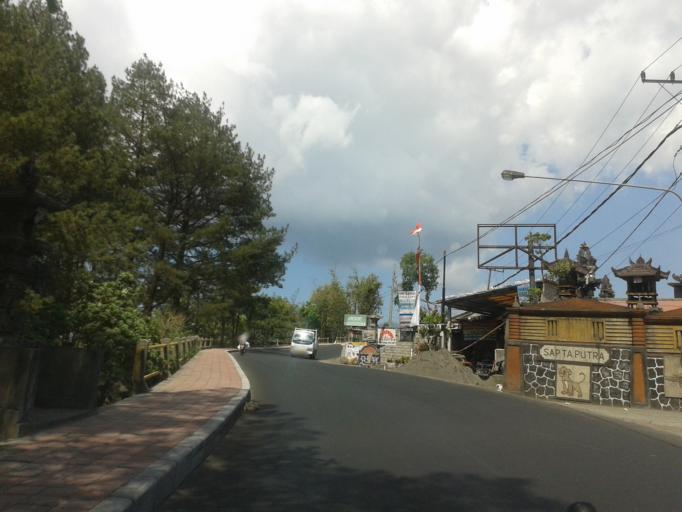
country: ID
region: Bali
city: Banjar Kedisan
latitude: -8.2783
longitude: 115.3540
